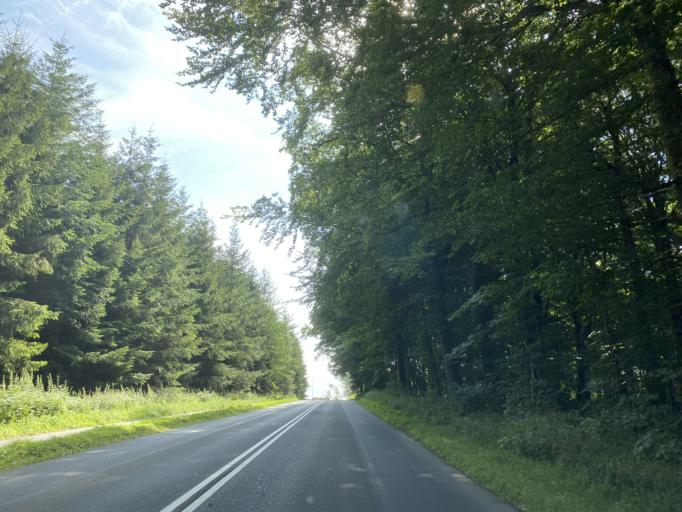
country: DK
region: Central Jutland
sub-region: Favrskov Kommune
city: Hammel
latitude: 56.2630
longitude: 9.8456
